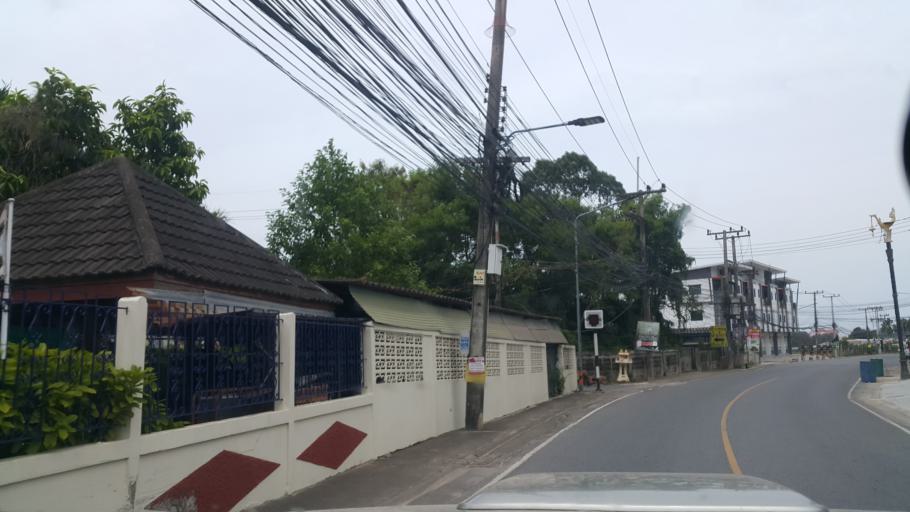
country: TH
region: Rayong
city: Ban Chang
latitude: 12.7180
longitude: 101.0492
